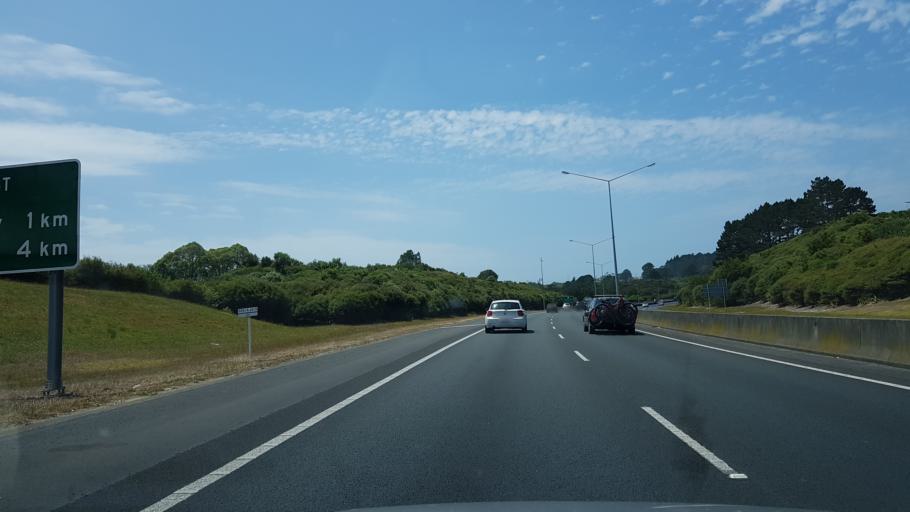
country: NZ
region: Auckland
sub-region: Auckland
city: Rothesay Bay
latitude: -36.7668
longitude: 174.6892
